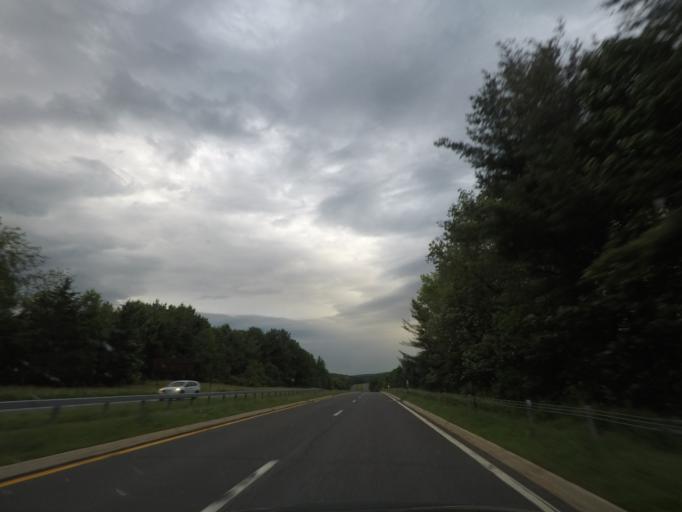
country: US
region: New York
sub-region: Columbia County
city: Philmont
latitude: 42.2154
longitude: -73.6347
